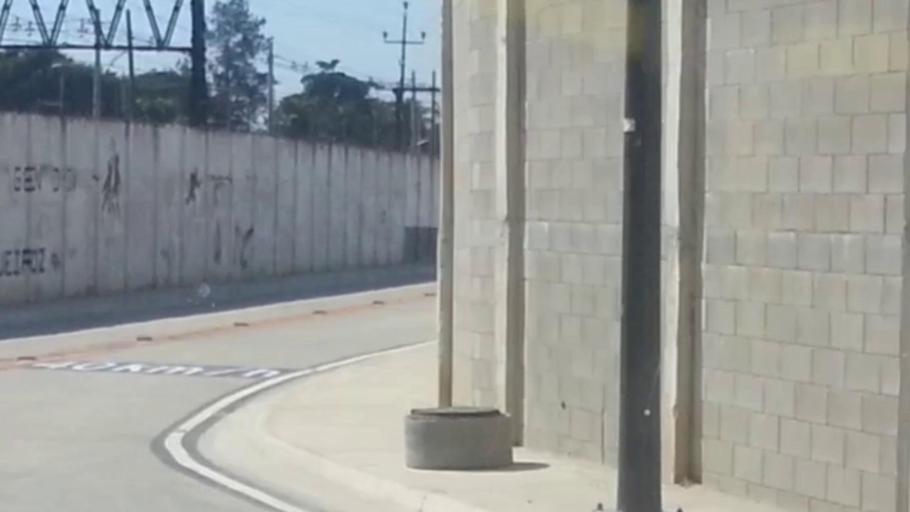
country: BR
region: Rio de Janeiro
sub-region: Nilopolis
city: Nilopolis
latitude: -22.8693
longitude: -43.4117
